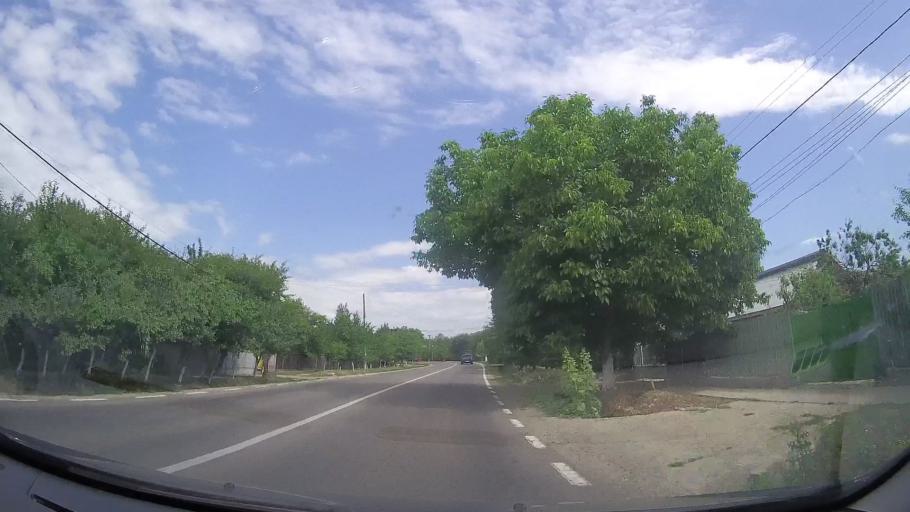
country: RO
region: Prahova
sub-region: Comuna Magurele
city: Magurele
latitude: 45.1109
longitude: 26.0355
